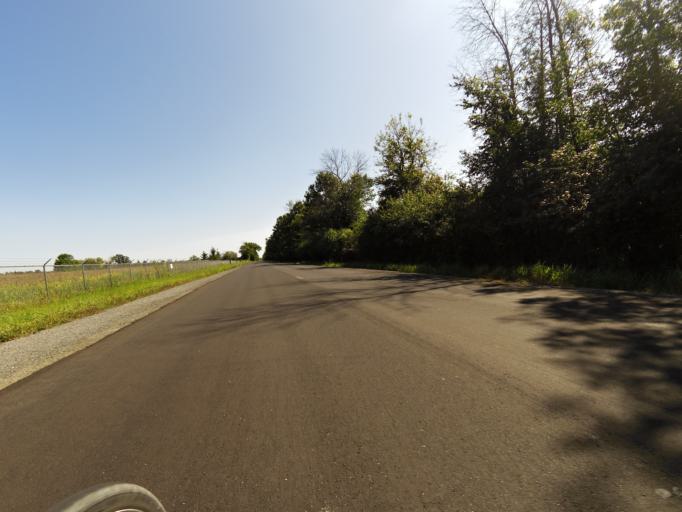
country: CA
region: Ontario
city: Bells Corners
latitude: 45.3701
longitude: -75.9281
